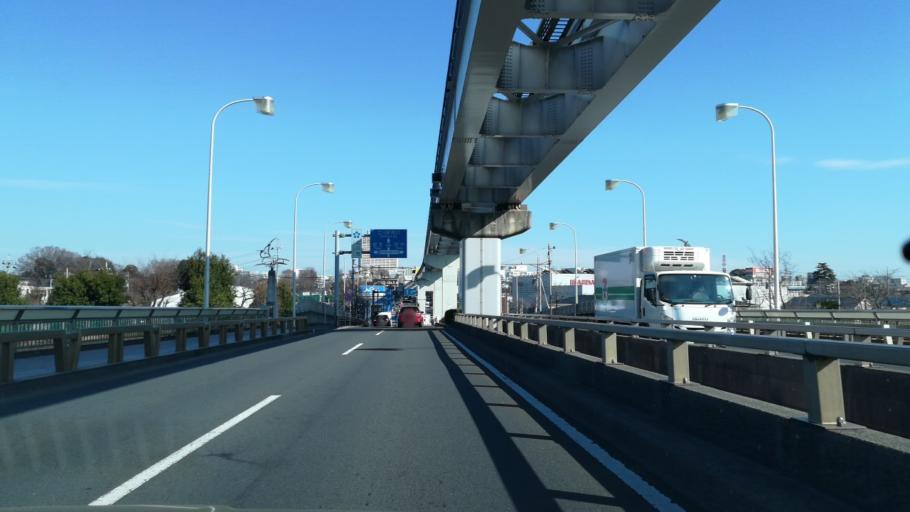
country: JP
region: Tokyo
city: Hino
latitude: 35.6858
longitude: 139.4076
